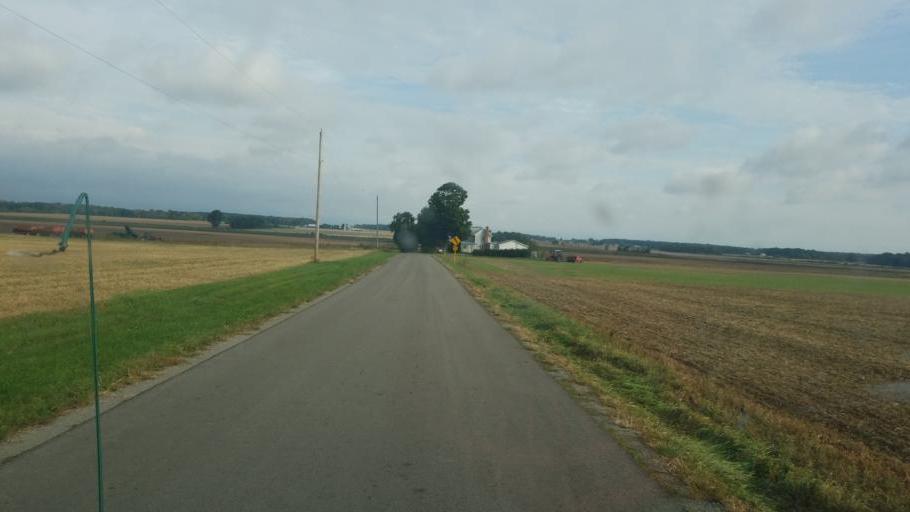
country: US
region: Ohio
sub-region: Wyandot County
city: Carey
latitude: 41.0124
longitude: -83.4489
